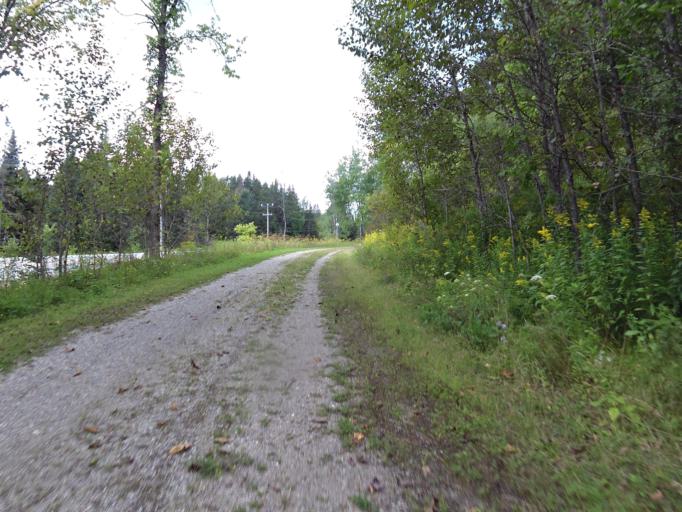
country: CA
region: Quebec
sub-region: Outaouais
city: Wakefield
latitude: 45.8454
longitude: -75.9831
